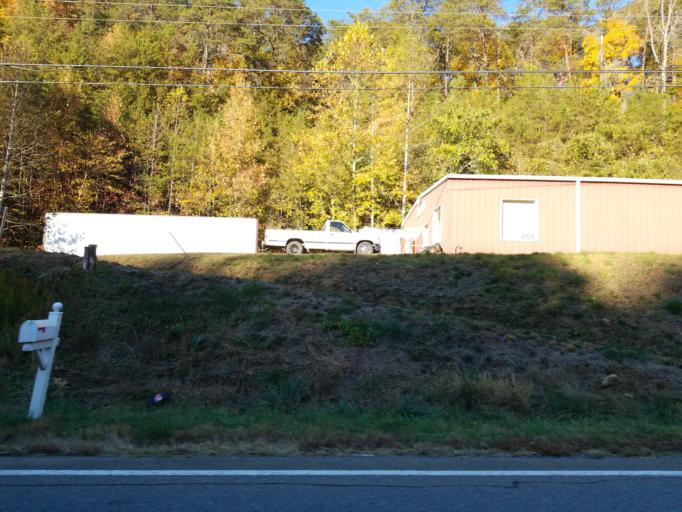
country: US
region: Georgia
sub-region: Gilmer County
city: Ellijay
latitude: 34.6870
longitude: -84.4631
